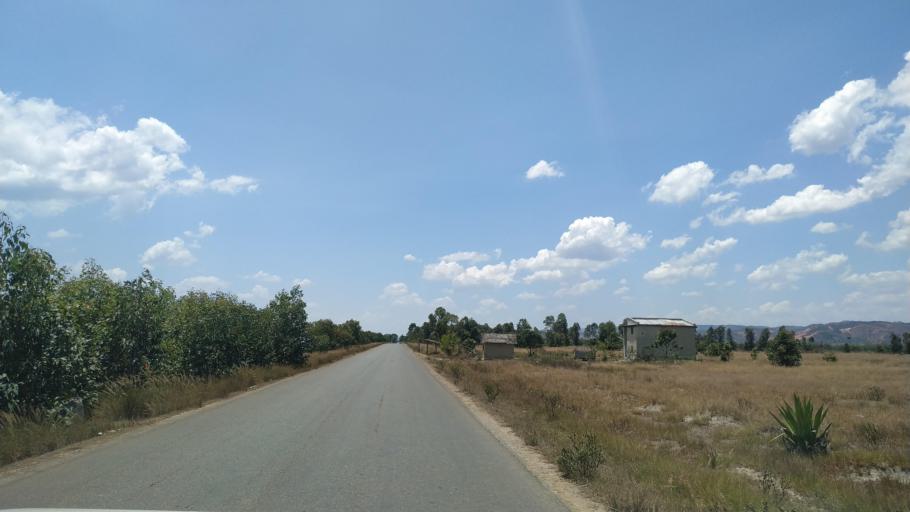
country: MG
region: Analamanga
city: Anjozorobe
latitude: -18.3150
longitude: 48.2651
